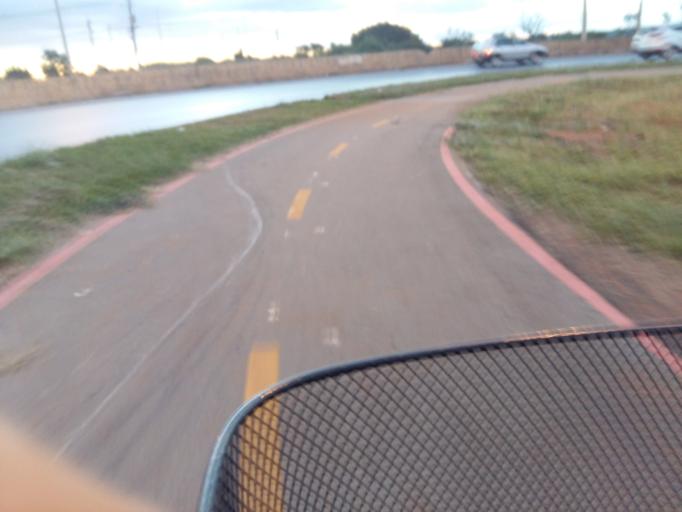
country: BR
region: Federal District
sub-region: Brasilia
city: Brasilia
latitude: -15.6871
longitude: -47.8580
